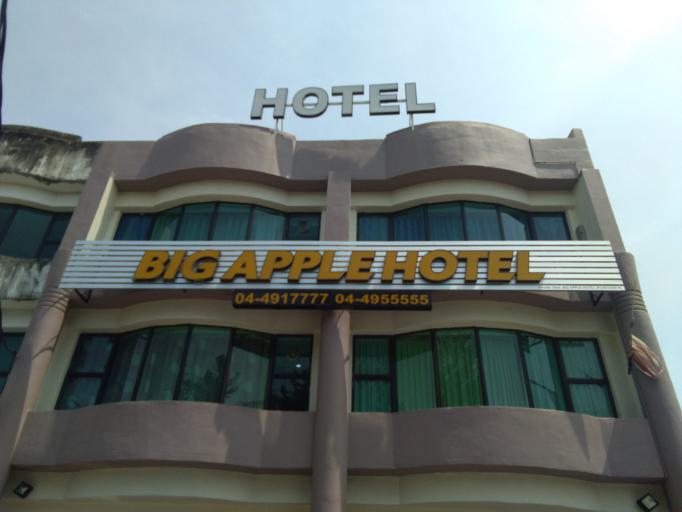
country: MY
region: Kedah
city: Kulim
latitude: 5.3667
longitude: 100.5516
